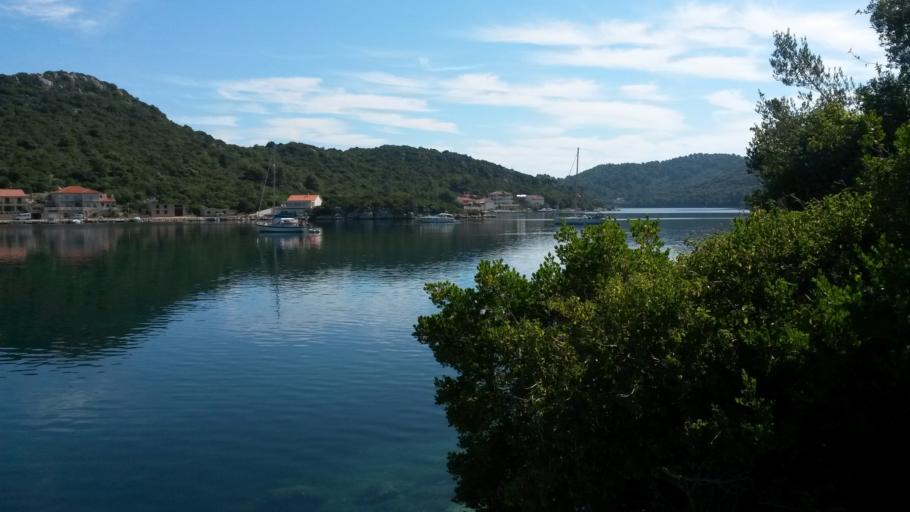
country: HR
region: Dubrovacko-Neretvanska
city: Smokvica
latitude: 42.7670
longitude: 16.8242
